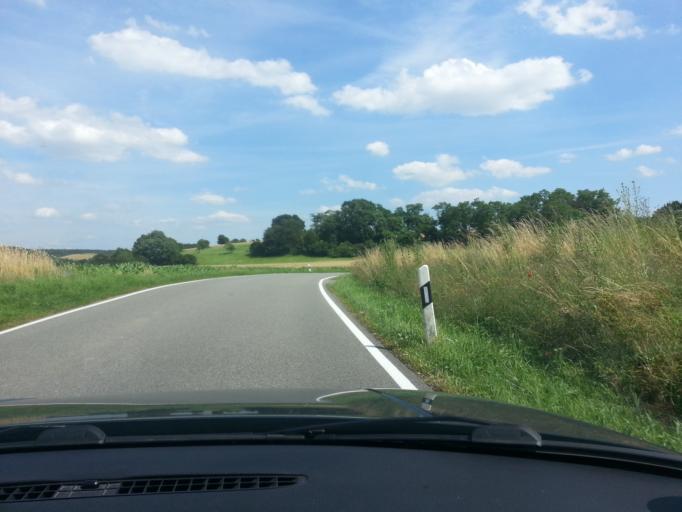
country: DE
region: Saarland
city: Blieskastel
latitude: 49.2209
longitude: 7.2703
